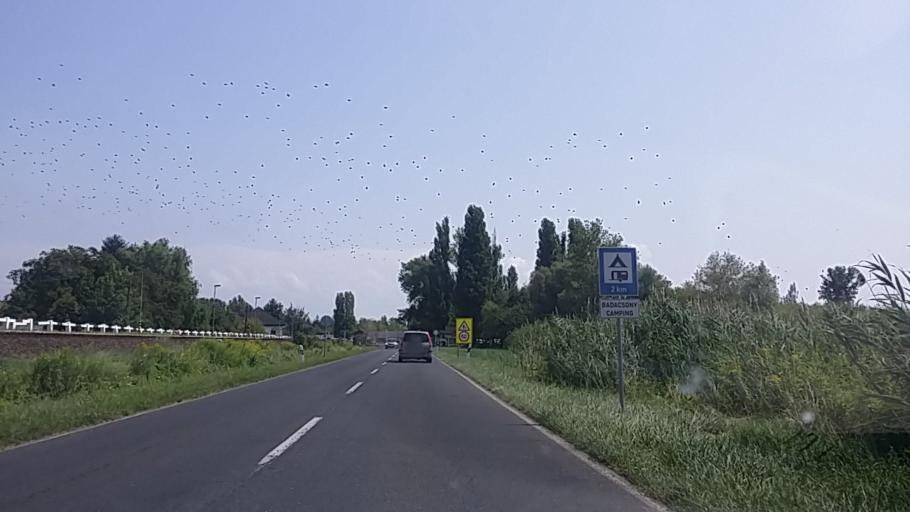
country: HU
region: Veszprem
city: Badacsonytomaj
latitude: 46.7920
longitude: 17.4721
